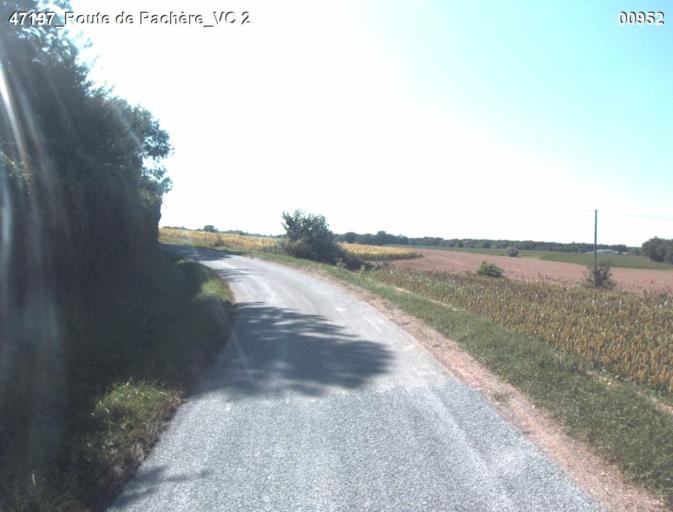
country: FR
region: Aquitaine
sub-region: Departement du Lot-et-Garonne
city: Laplume
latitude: 44.0919
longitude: 0.4614
